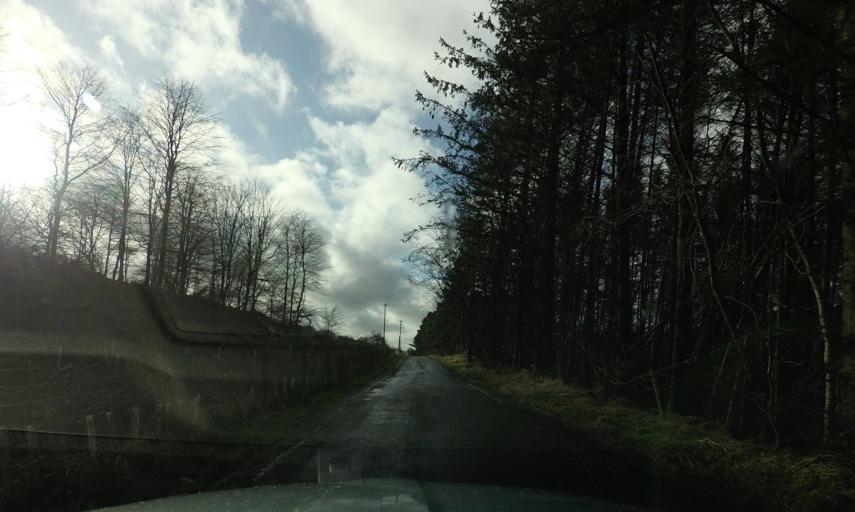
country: GB
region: Scotland
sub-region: West Lothian
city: Bathgate
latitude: 55.9322
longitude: -3.6122
